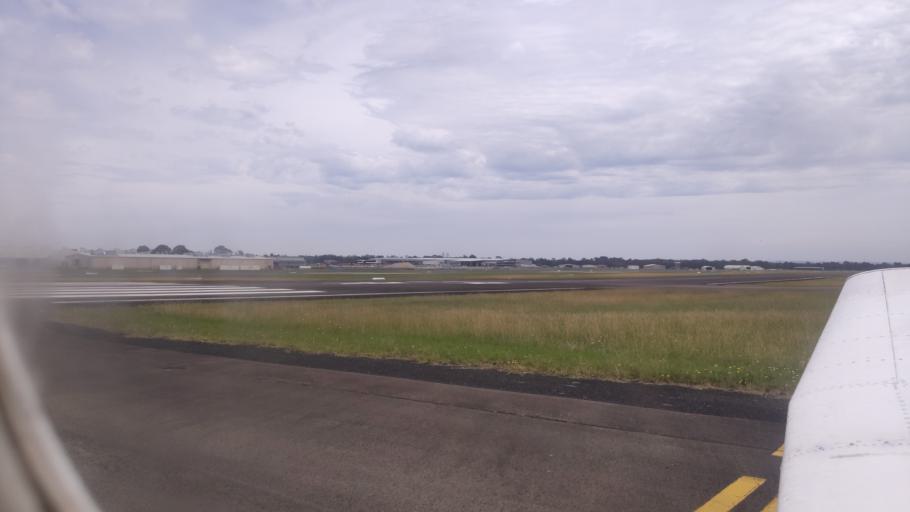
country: AU
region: New South Wales
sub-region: Bankstown
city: Milperra
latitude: -33.9249
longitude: 150.9957
